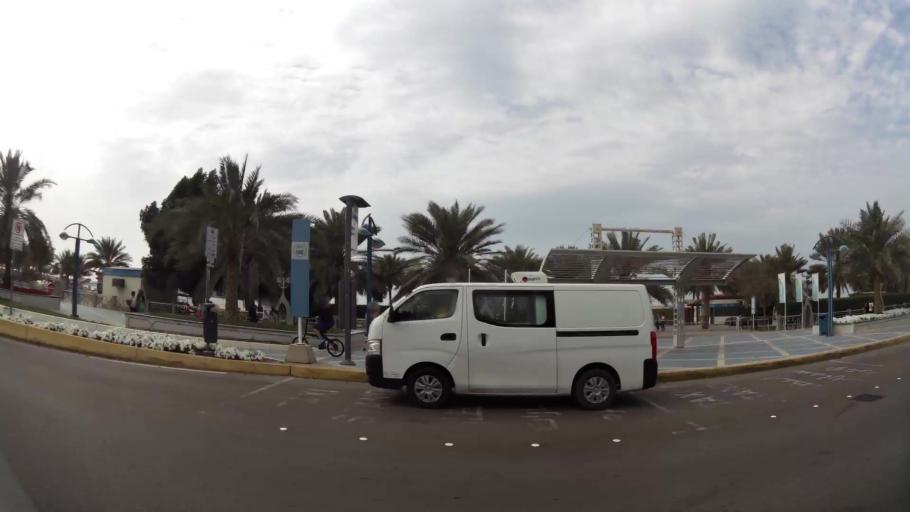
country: AE
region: Abu Dhabi
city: Abu Dhabi
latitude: 24.4743
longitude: 54.3424
